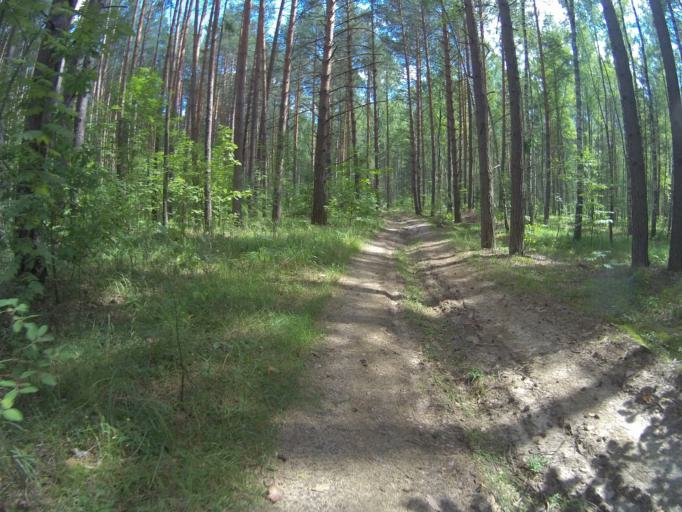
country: RU
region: Vladimir
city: Raduzhnyy
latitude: 56.0595
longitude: 40.3455
